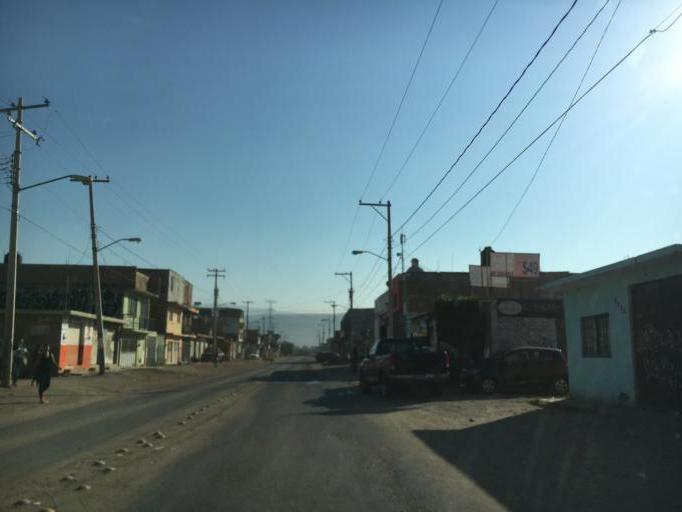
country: MX
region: Guanajuato
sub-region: Leon
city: Fraccionamiento Paraiso Real
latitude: 21.1008
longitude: -101.6008
